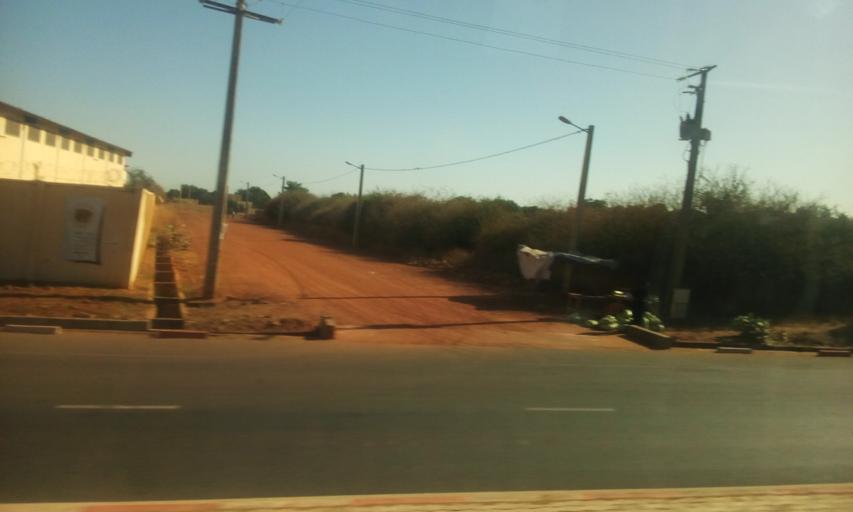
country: ML
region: Segou
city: Segou
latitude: 13.4159
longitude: -6.3140
